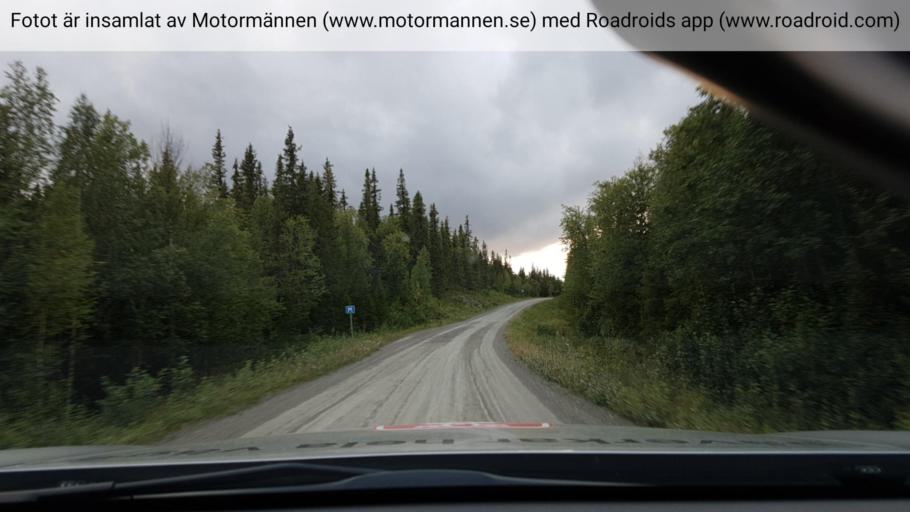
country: SE
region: Vaesterbotten
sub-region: Vilhelmina Kommun
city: Sjoberg
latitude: 65.4933
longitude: 15.4964
